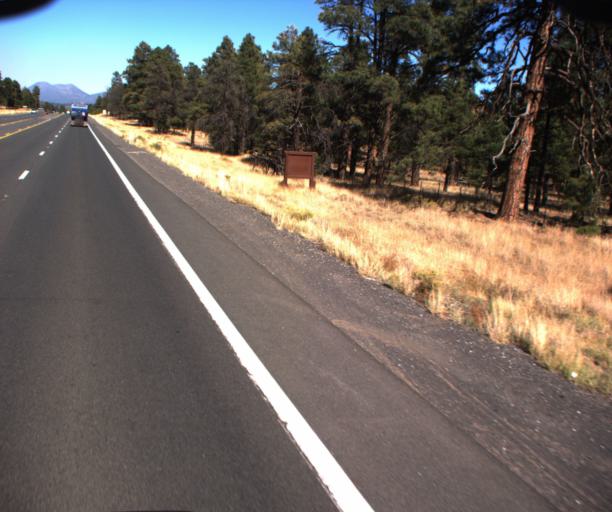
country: US
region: Arizona
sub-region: Coconino County
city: Flagstaff
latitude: 35.2763
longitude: -111.5431
